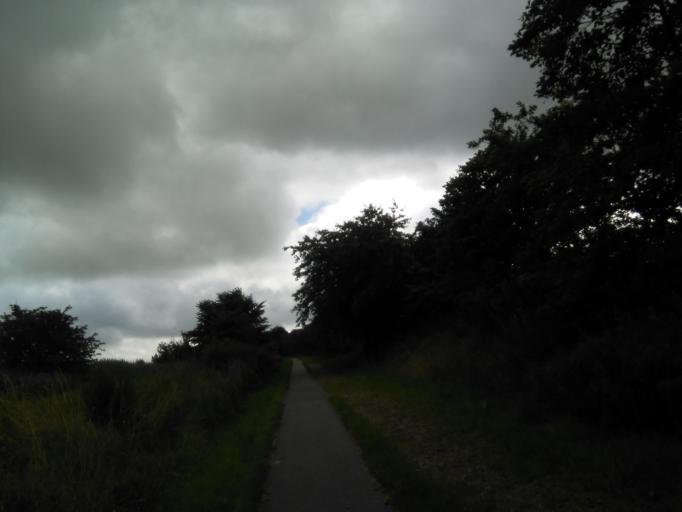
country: DK
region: Central Jutland
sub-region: Silkeborg Kommune
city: Virklund
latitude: 56.0889
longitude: 9.5313
